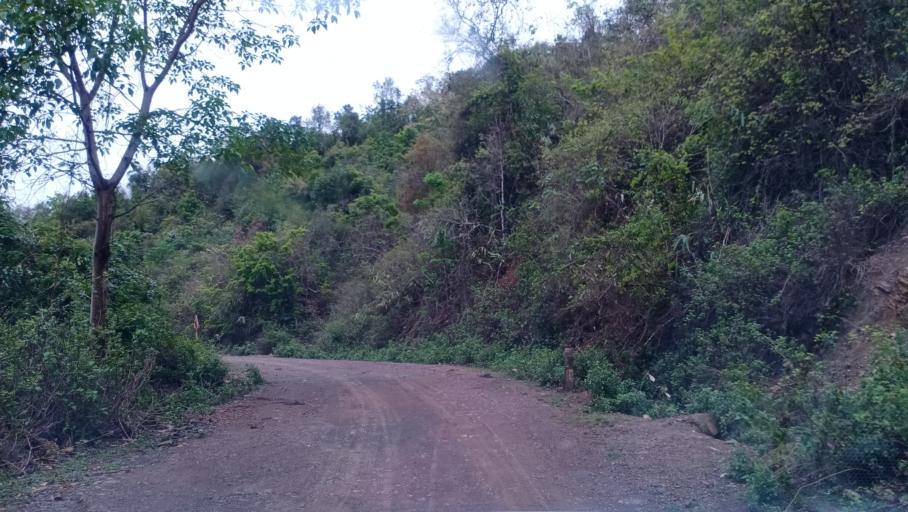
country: LA
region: Phongsali
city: Phongsali
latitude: 21.3482
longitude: 102.0975
